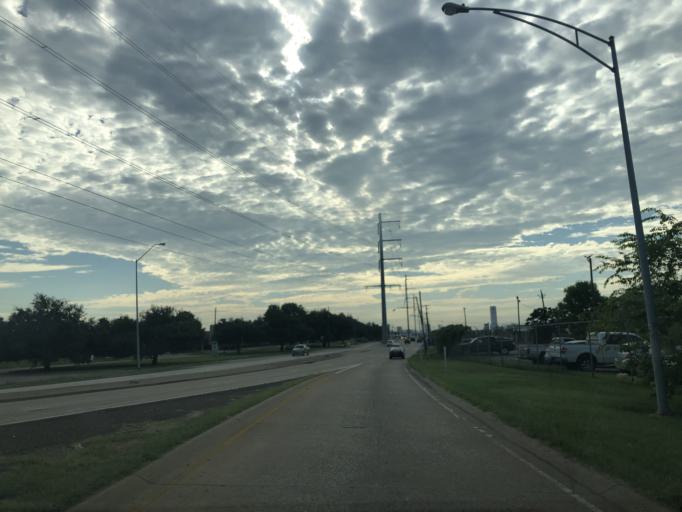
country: US
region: Texas
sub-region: Dallas County
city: Irving
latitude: 32.8081
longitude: -96.8996
